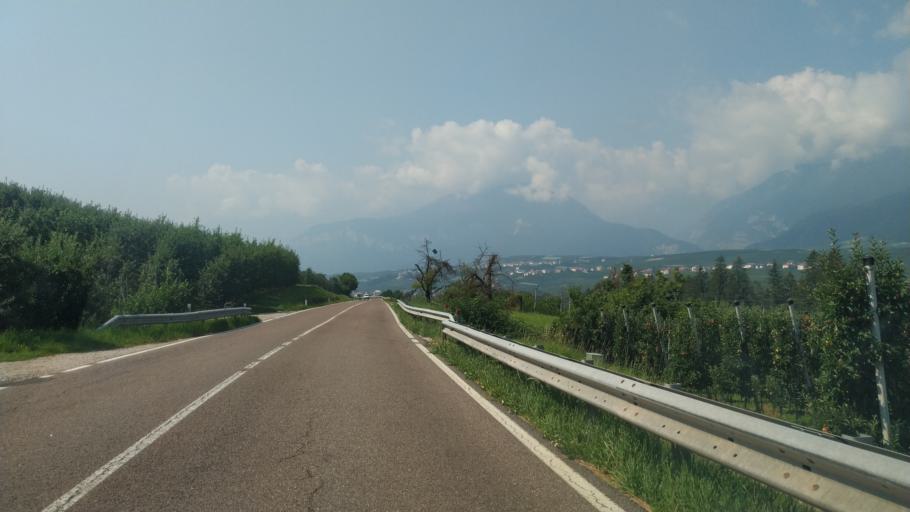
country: IT
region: Trentino-Alto Adige
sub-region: Provincia di Trento
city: Sanzeno
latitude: 46.3530
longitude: 11.0677
